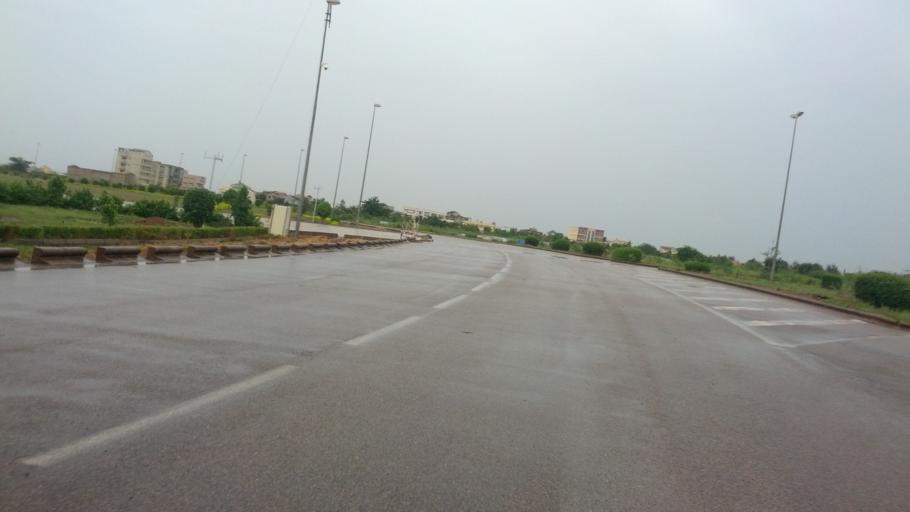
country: BF
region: Centre
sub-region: Kadiogo Province
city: Ouagadougou
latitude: 12.3097
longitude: -1.5034
